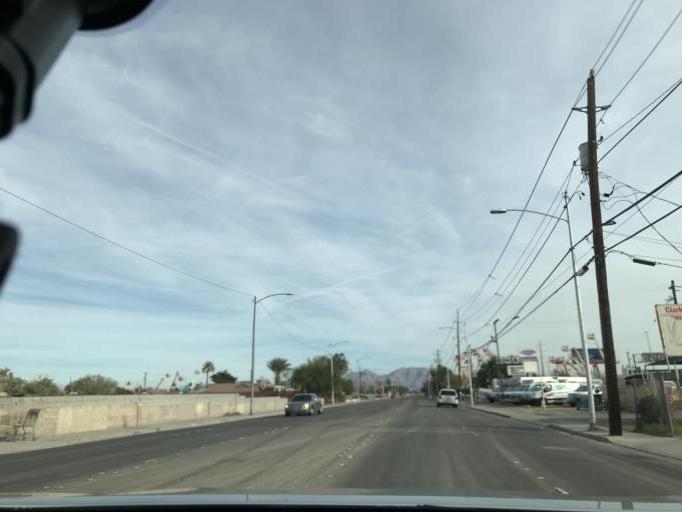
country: US
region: Nevada
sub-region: Clark County
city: Las Vegas
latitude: 36.1771
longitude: -115.1695
